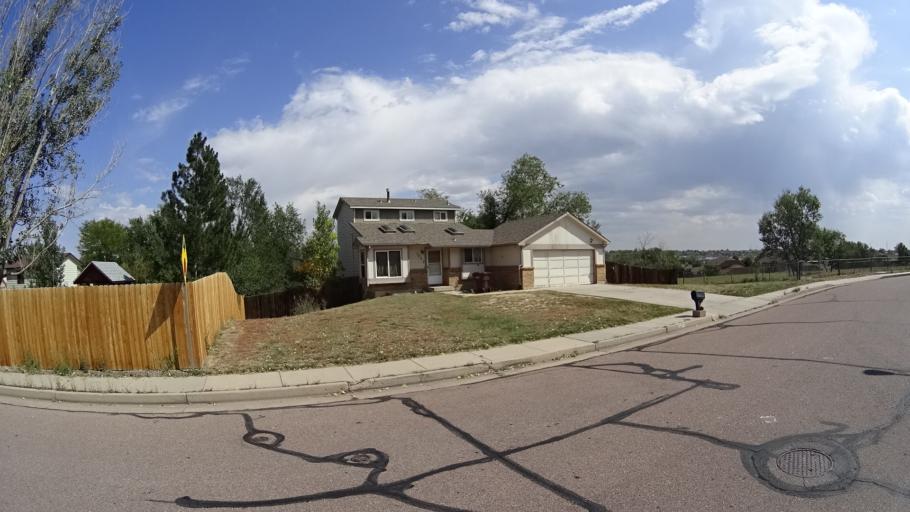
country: US
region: Colorado
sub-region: El Paso County
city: Cimarron Hills
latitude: 38.8581
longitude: -104.7282
